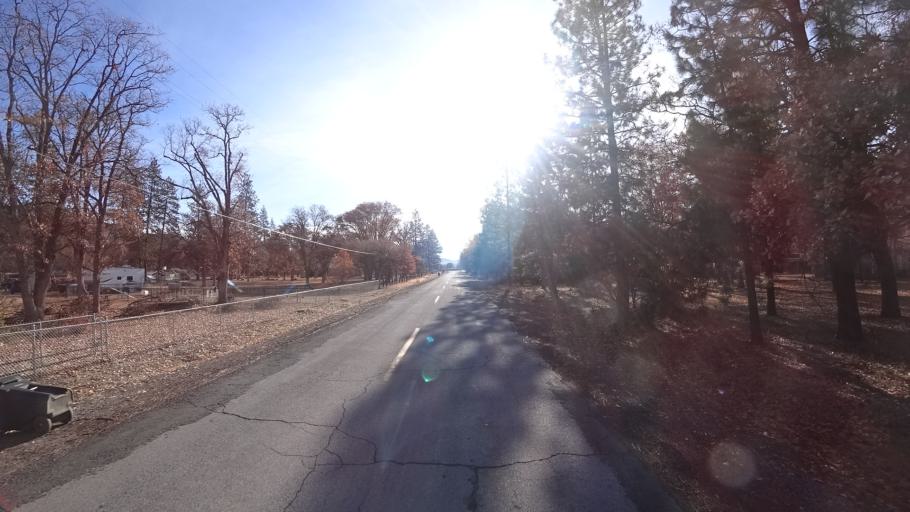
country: US
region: California
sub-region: Siskiyou County
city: Yreka
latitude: 41.6657
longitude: -122.6046
